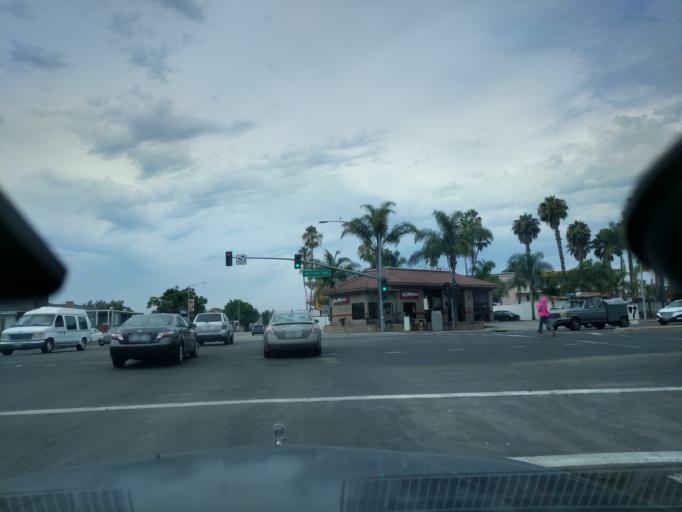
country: US
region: California
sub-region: Santa Barbara County
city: Goleta
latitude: 34.4363
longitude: -119.8308
